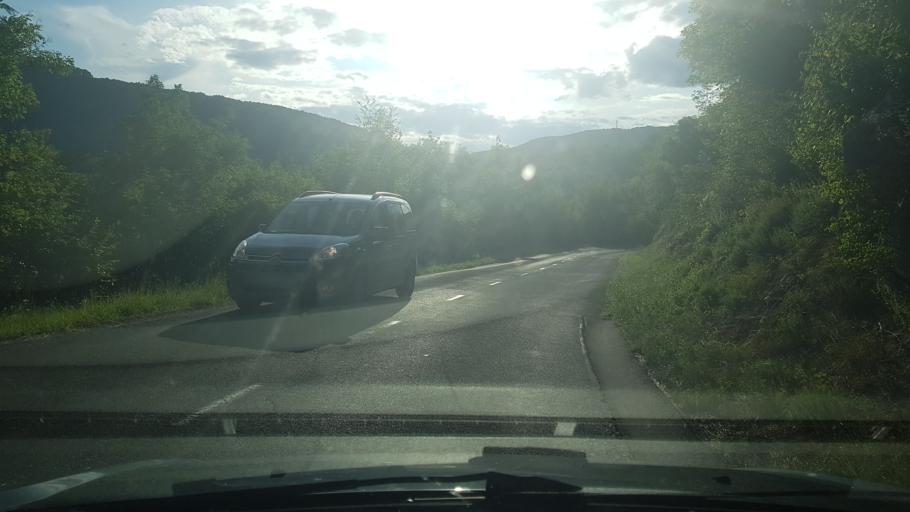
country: SI
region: Nova Gorica
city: Solkan
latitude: 46.0092
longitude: 13.6781
